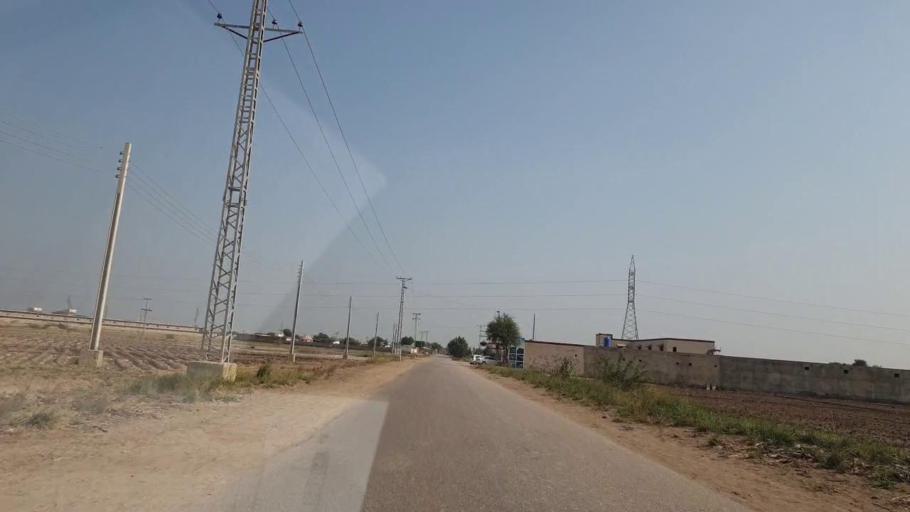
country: PK
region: Sindh
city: Matiari
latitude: 25.5042
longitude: 68.4313
